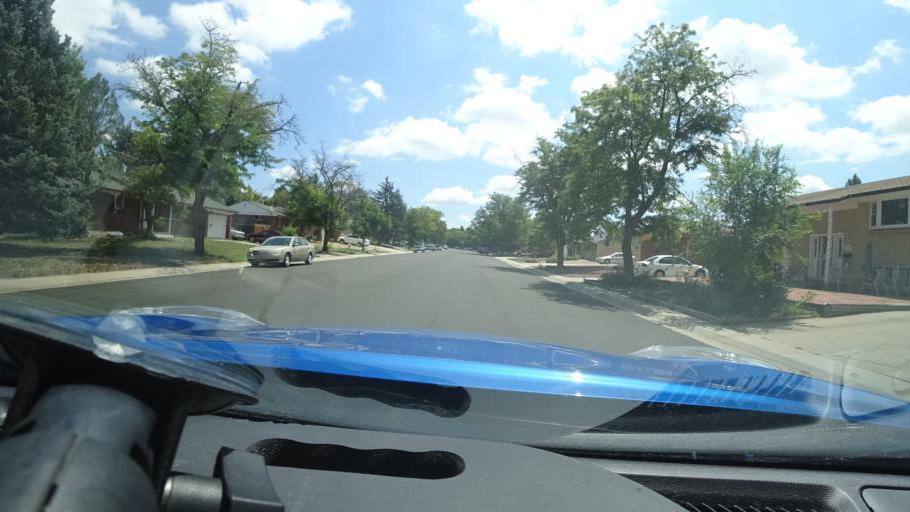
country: US
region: Colorado
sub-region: Adams County
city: Aurora
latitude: 39.7070
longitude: -104.8513
